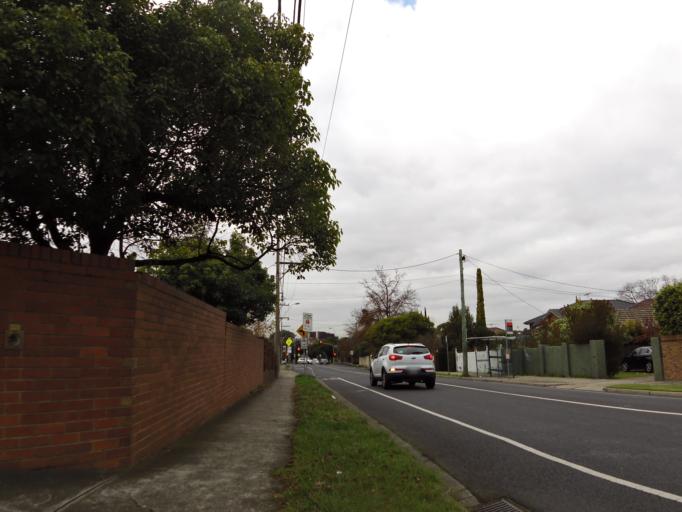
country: AU
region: Victoria
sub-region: Banyule
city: Bellfield
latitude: -37.7668
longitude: 145.0335
